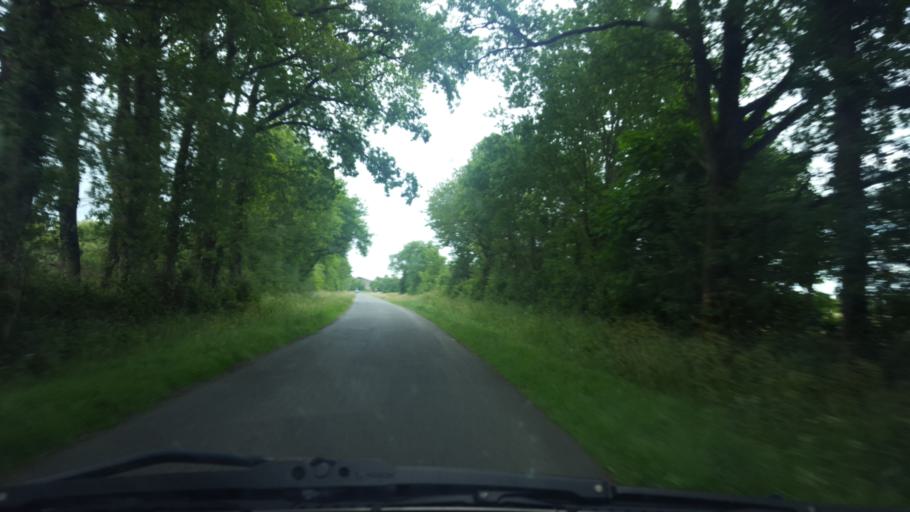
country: FR
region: Pays de la Loire
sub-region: Departement de la Loire-Atlantique
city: Saint-Philbert-de-Grand-Lieu
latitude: 47.0110
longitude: -1.6749
